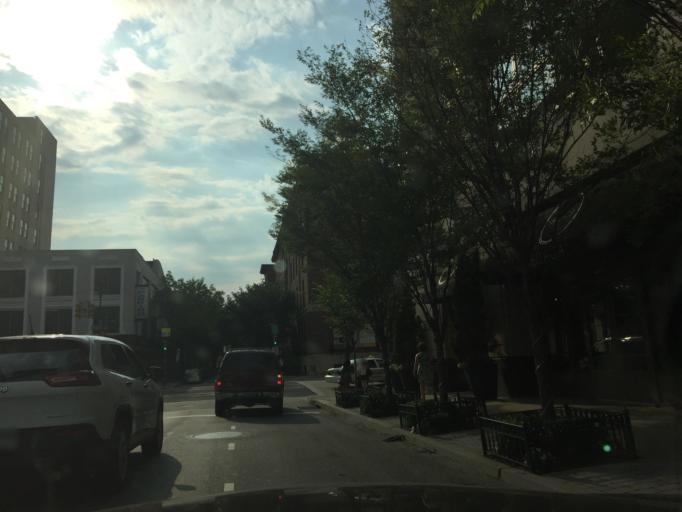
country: US
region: Pennsylvania
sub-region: Philadelphia County
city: Philadelphia
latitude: 39.9456
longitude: -75.1656
